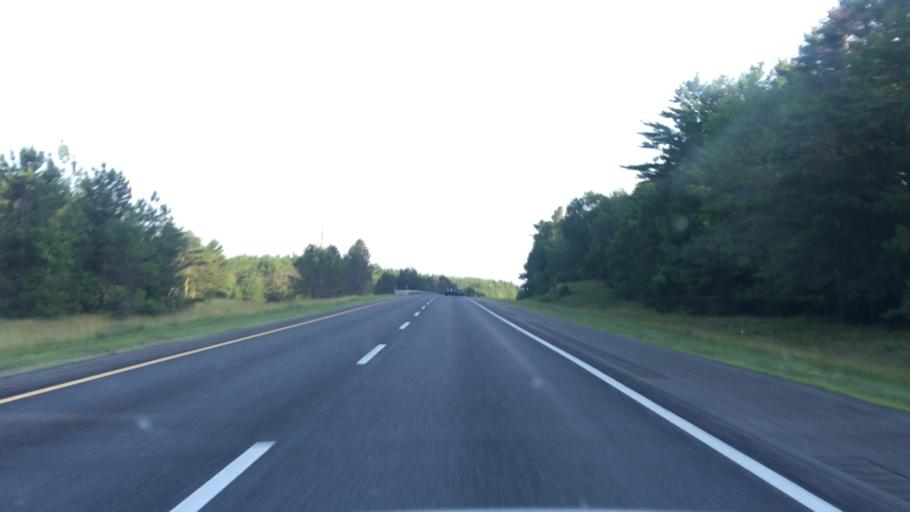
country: US
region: Maine
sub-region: Sagadahoc County
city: Topsham
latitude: 43.9893
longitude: -69.9404
